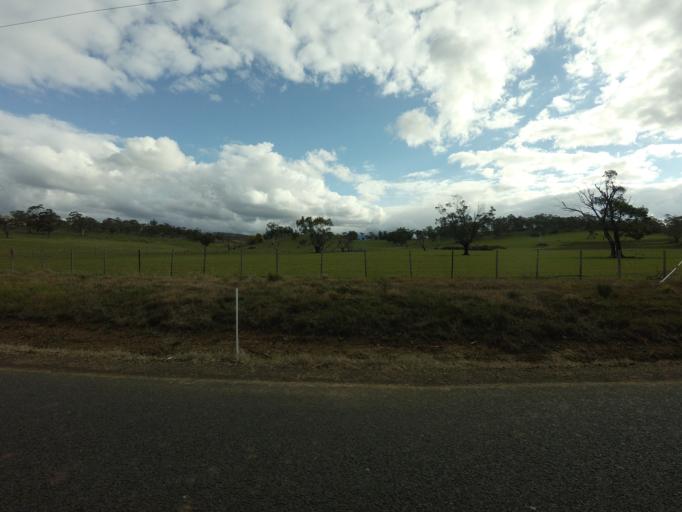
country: AU
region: Tasmania
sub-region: Northern Midlands
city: Evandale
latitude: -41.8773
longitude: 147.3050
